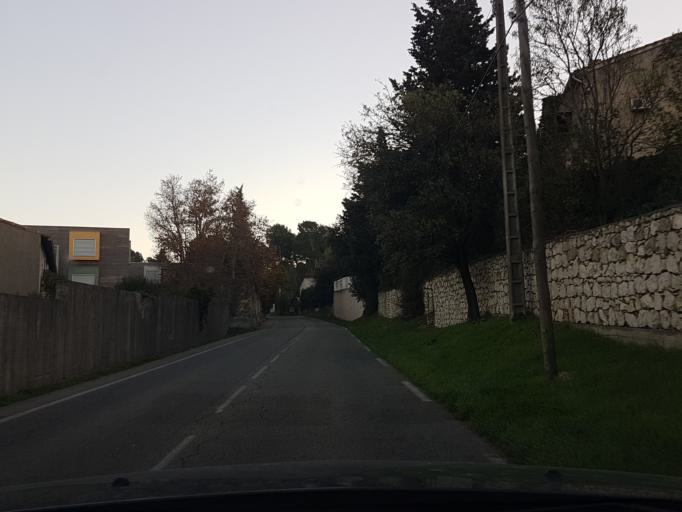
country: FR
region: Provence-Alpes-Cote d'Azur
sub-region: Departement du Vaucluse
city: Vedene
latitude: 43.9851
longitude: 4.8979
